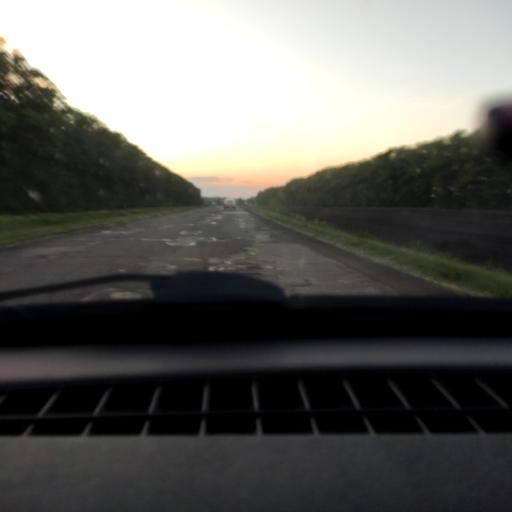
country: RU
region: Bashkortostan
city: Karmaskaly
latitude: 54.3924
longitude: 56.1724
